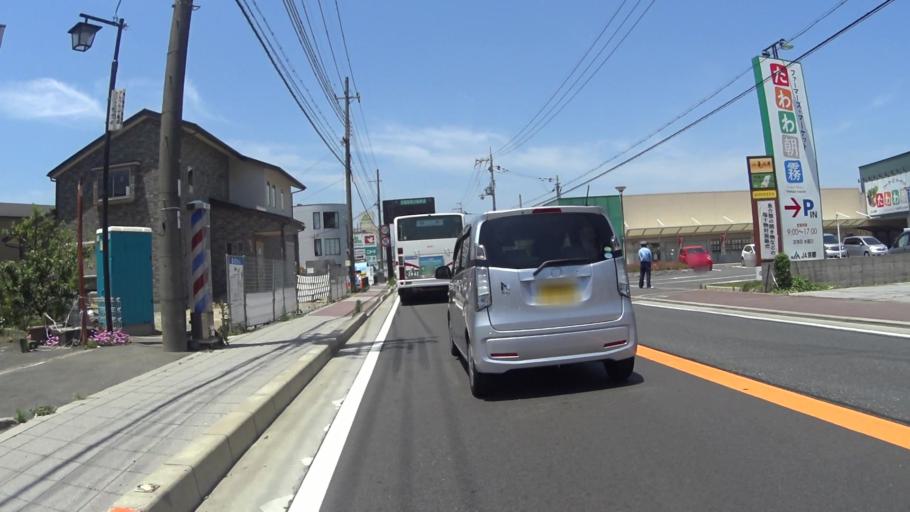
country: JP
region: Kyoto
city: Kameoka
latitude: 35.0016
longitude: 135.6053
